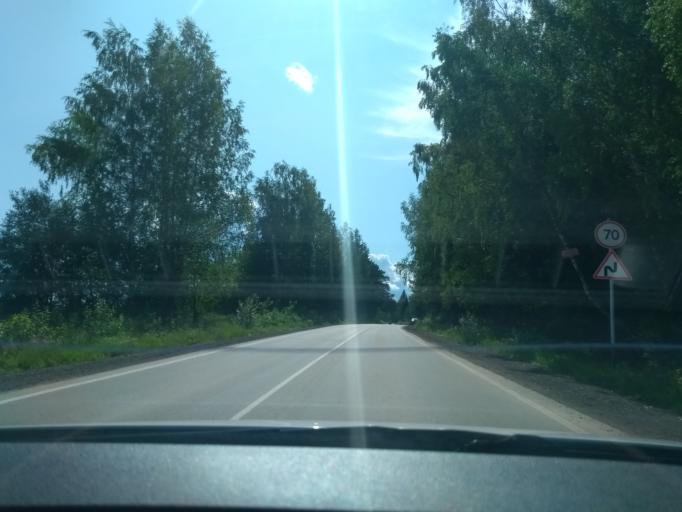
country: RU
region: Perm
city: Lobanovo
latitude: 57.8348
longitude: 56.3998
